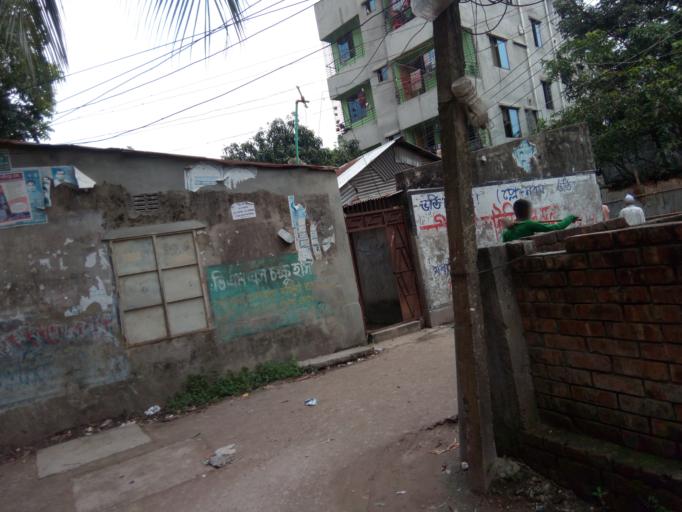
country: BD
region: Dhaka
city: Paltan
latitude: 23.7475
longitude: 90.4495
